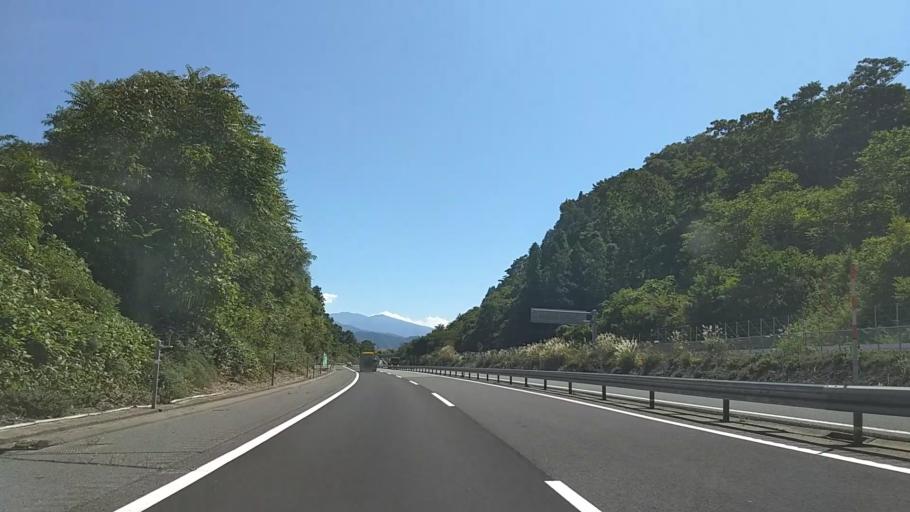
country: JP
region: Nagano
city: Nakano
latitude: 36.7794
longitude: 138.3174
